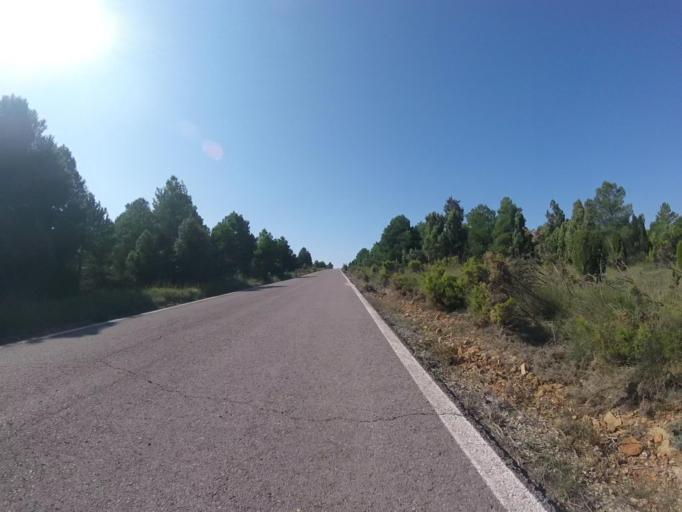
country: ES
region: Valencia
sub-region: Provincia de Castello
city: Benafigos
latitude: 40.2830
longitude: -0.2387
